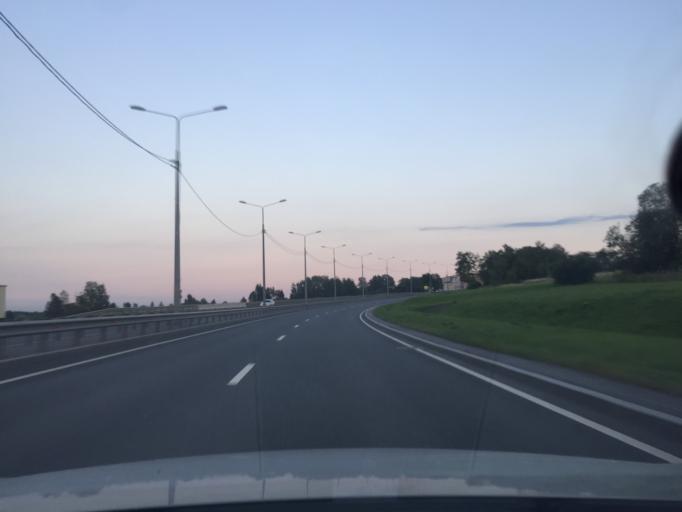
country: RU
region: St.-Petersburg
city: Aleksandrovskaya
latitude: 59.7717
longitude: 30.3415
